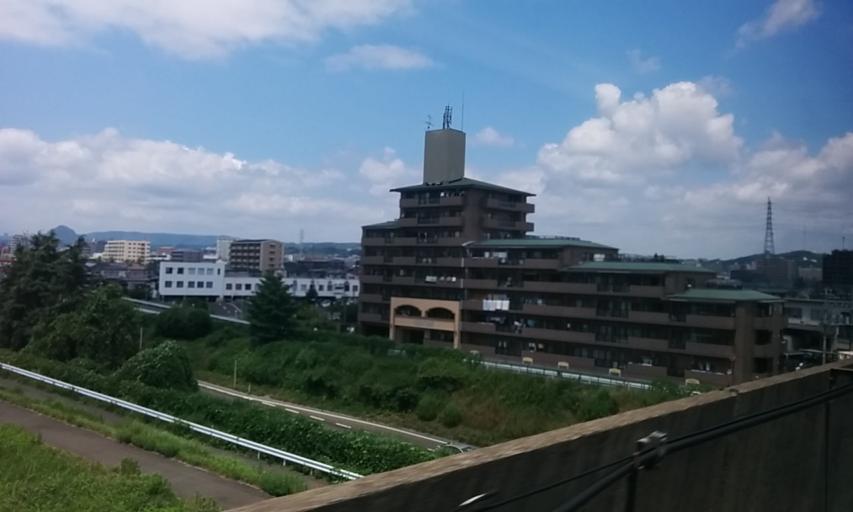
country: JP
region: Miyagi
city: Sendai
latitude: 38.2083
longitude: 140.8829
